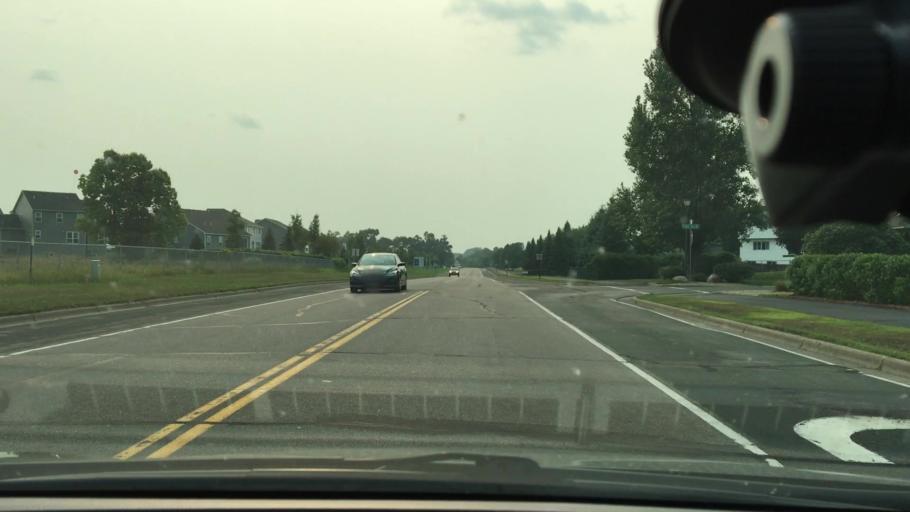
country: US
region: Minnesota
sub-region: Wright County
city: Otsego
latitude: 45.2633
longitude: -93.5671
